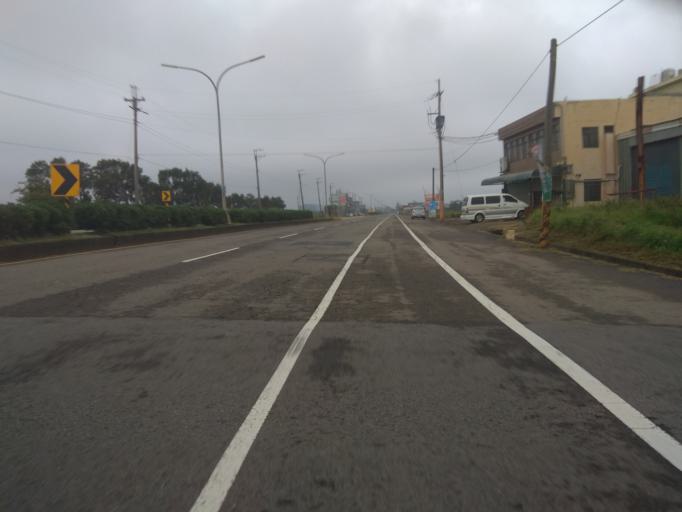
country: TW
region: Taiwan
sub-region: Hsinchu
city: Zhubei
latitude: 25.0242
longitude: 121.0817
